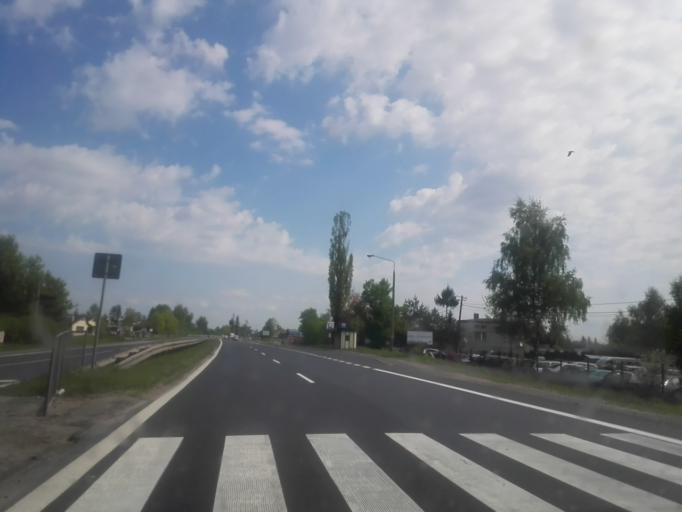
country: PL
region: Masovian Voivodeship
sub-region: Powiat pruszkowski
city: Nadarzyn
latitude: 52.0783
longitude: 20.7860
